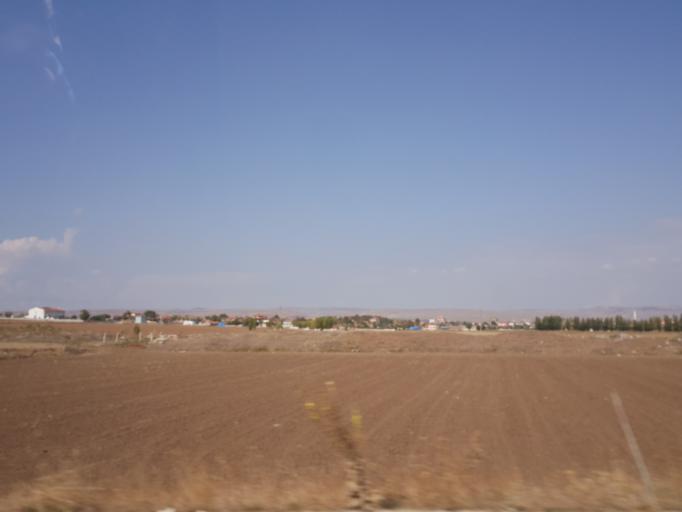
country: TR
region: Corum
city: Alaca
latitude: 40.1499
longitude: 34.8459
